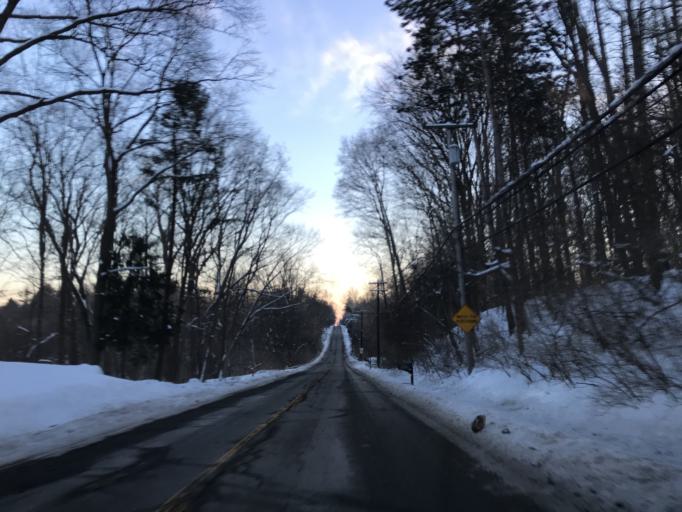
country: US
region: Michigan
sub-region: Oakland County
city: Bingham Farms
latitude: 42.4690
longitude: -83.2986
